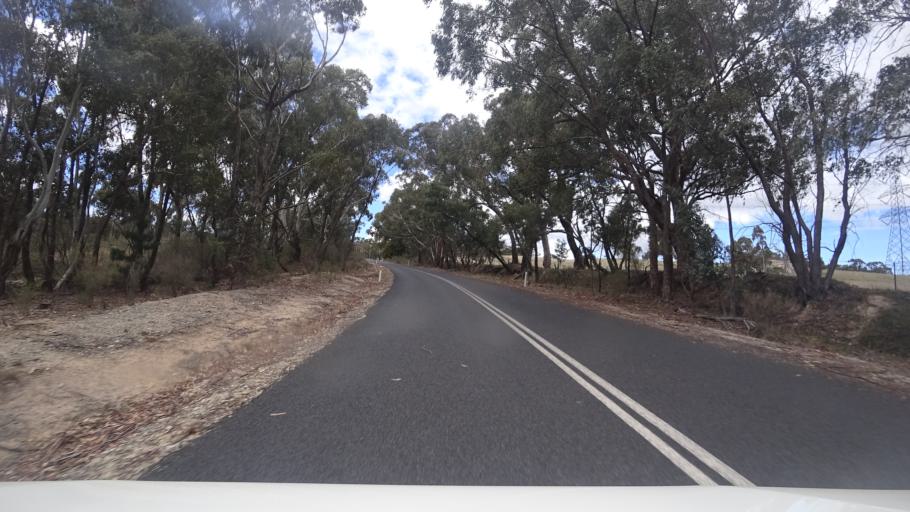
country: AU
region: New South Wales
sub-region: Oberon
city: Oberon
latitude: -33.6221
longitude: 149.8876
